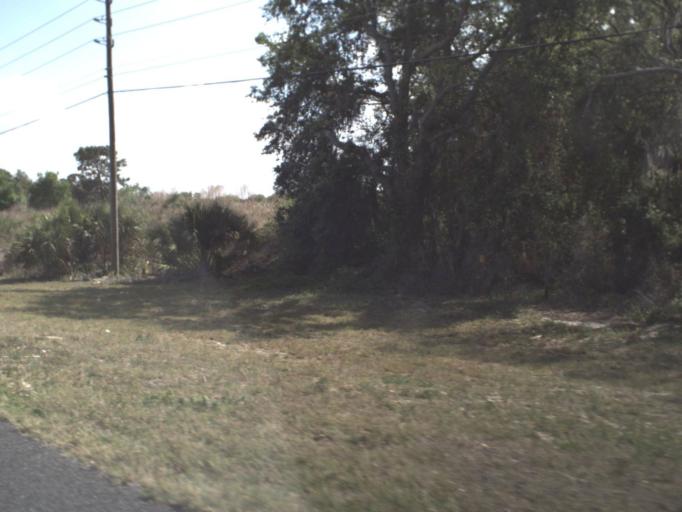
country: US
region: Florida
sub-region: Lake County
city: Hawthorne
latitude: 28.7342
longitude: -81.8684
